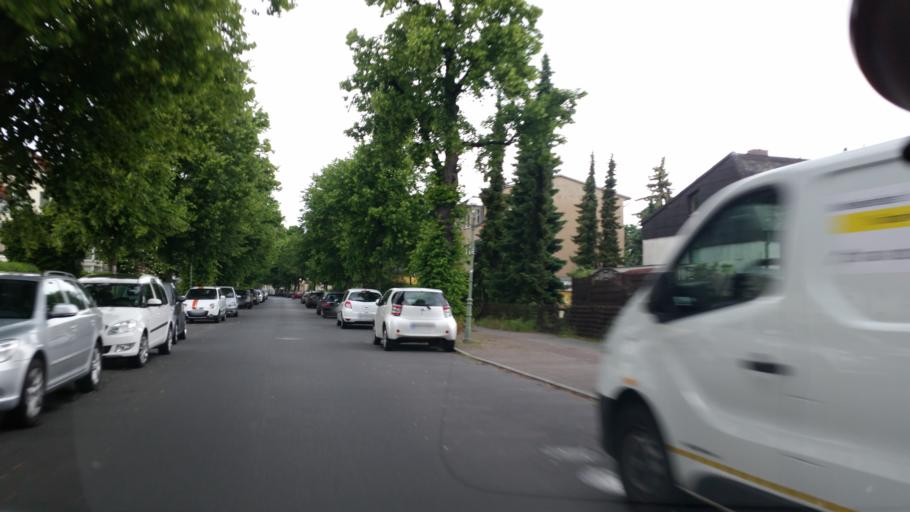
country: DE
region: Berlin
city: Lichtenrade
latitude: 52.3957
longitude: 13.4110
